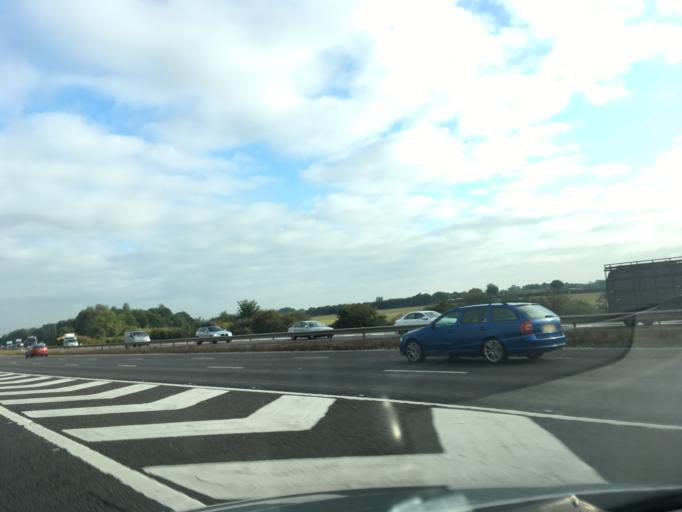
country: GB
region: England
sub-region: Oxfordshire
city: Bicester
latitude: 51.8722
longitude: -1.2008
